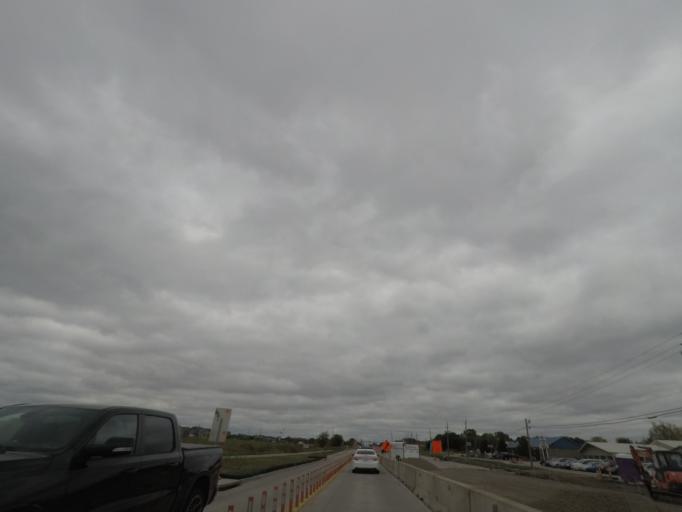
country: US
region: Iowa
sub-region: Polk County
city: Ankeny
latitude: 41.7127
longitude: -93.6006
